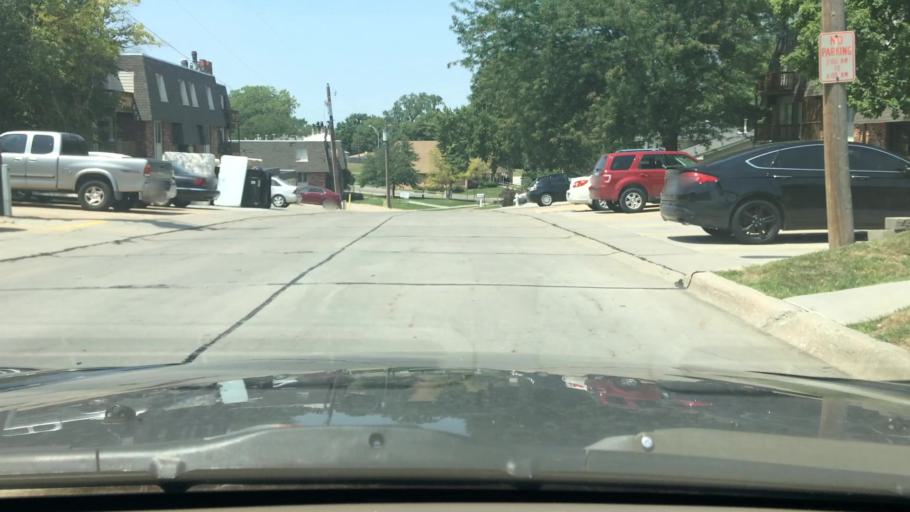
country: US
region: Nebraska
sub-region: Sarpy County
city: La Vista
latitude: 41.1920
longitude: -96.0407
